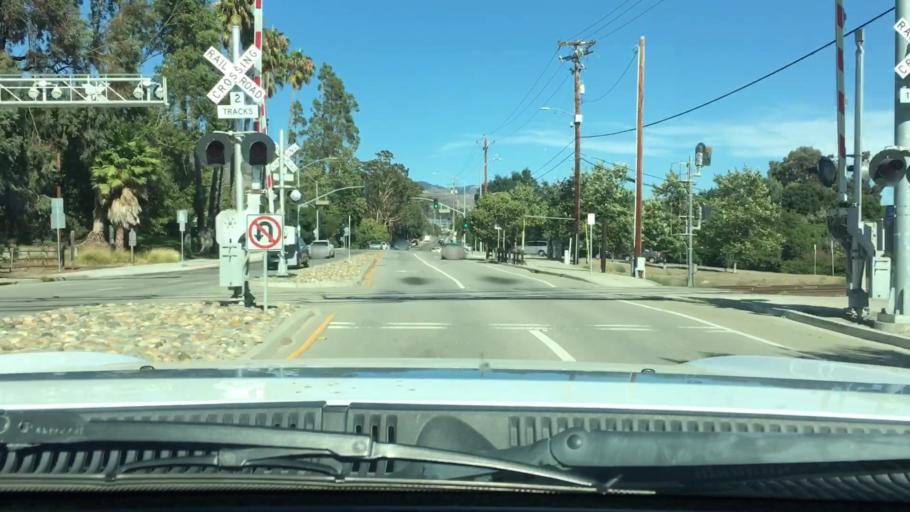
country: US
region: California
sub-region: San Luis Obispo County
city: San Luis Obispo
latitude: 35.2613
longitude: -120.6448
